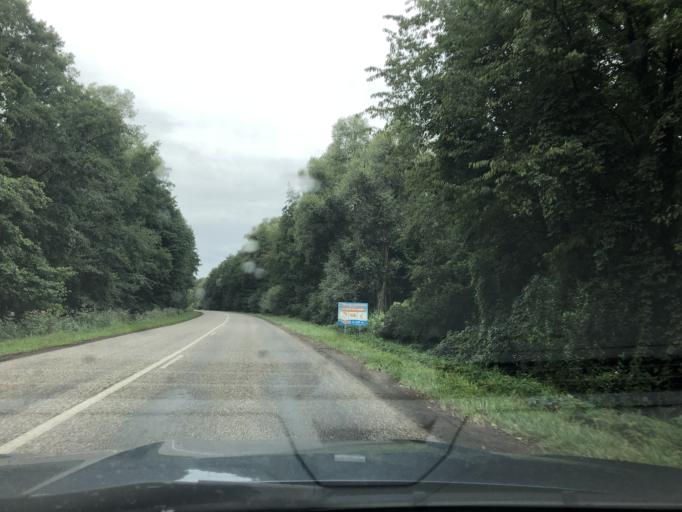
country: DE
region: Rheinland-Pfalz
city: Berg
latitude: 48.9703
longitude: 8.1790
